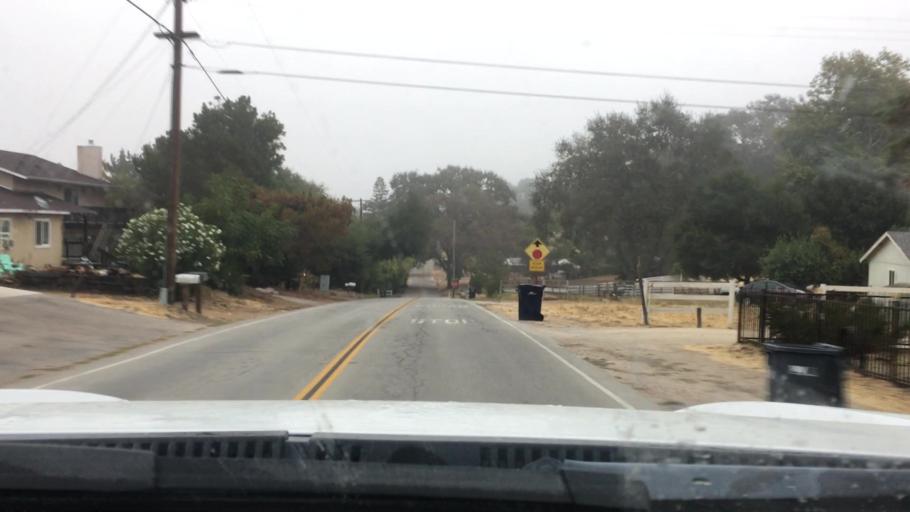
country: US
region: California
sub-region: San Luis Obispo County
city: Atascadero
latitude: 35.4906
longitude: -120.6850
